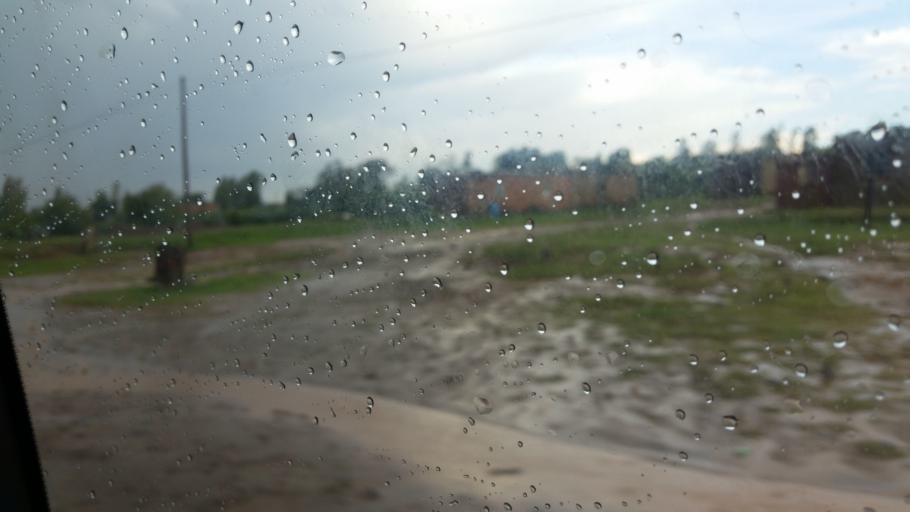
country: LS
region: Mafeteng
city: Mafeteng
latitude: -29.7549
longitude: 27.1298
